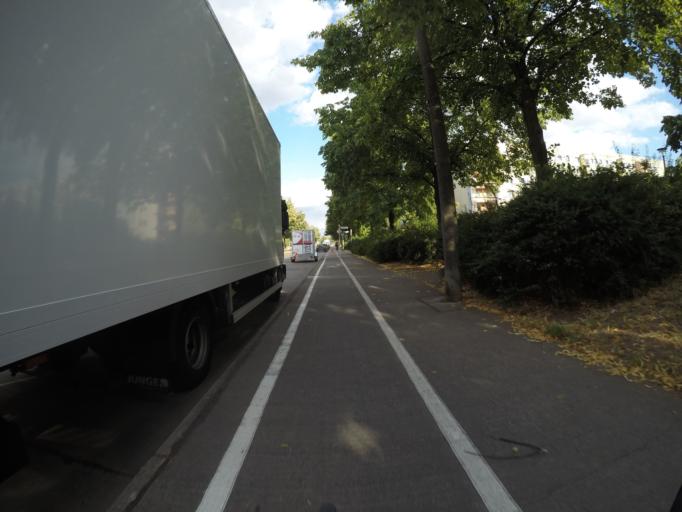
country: DE
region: Berlin
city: Hellersdorf
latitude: 52.5325
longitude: 13.6119
